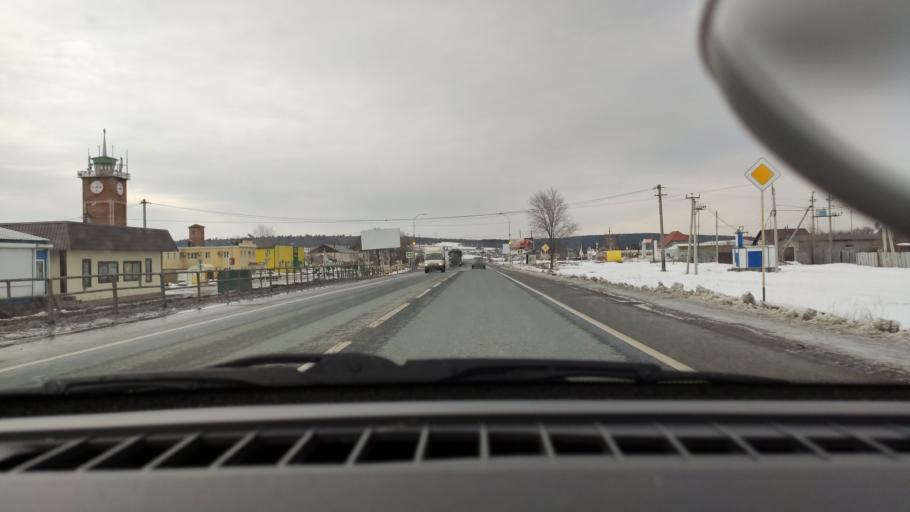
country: RU
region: Samara
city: Kurumoch
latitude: 53.4844
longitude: 50.0269
